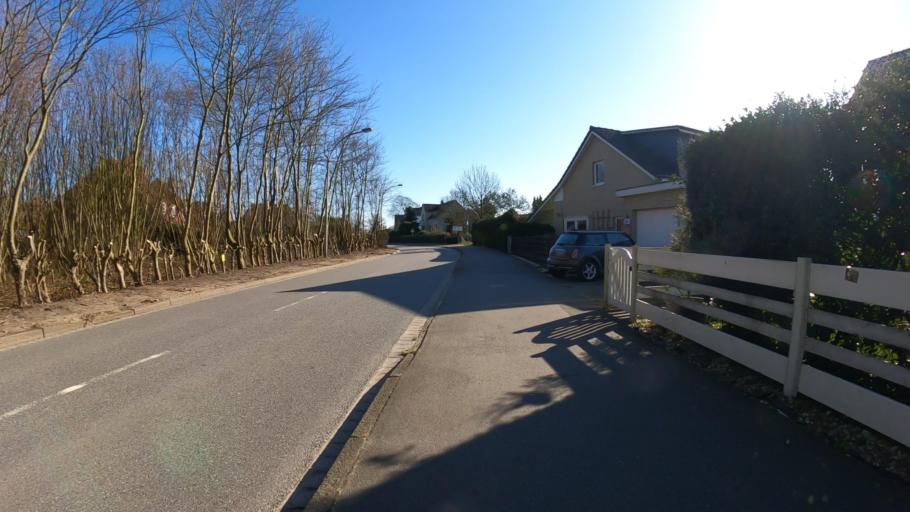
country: DE
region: Schleswig-Holstein
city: Rellingen
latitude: 53.6410
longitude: 9.8017
